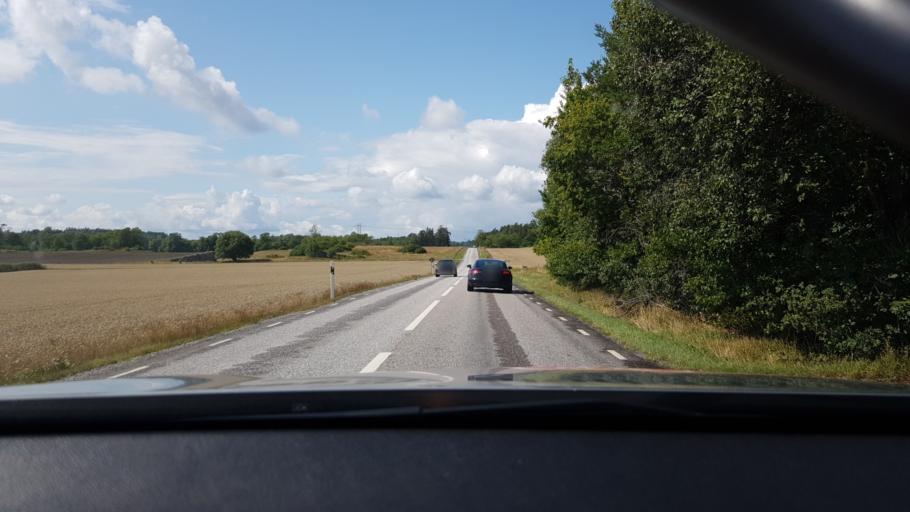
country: SE
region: Stockholm
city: Stenhamra
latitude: 59.2909
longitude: 17.6957
